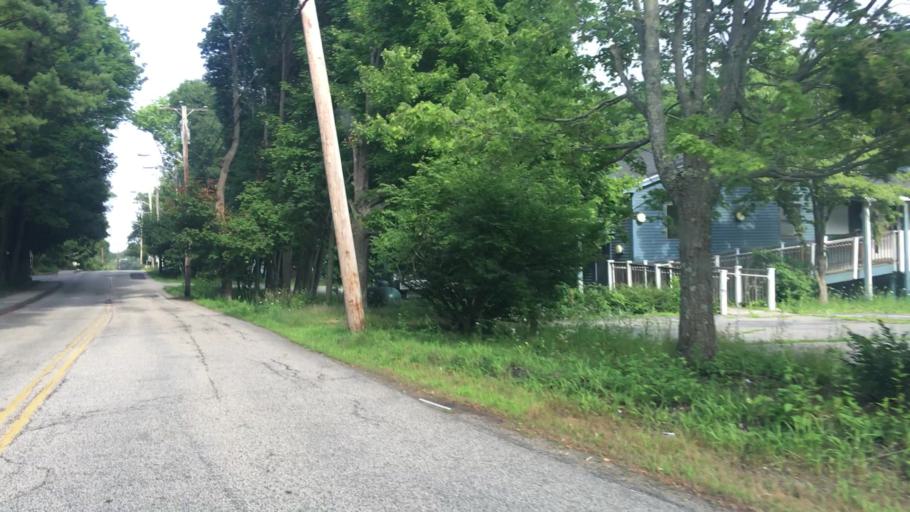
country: US
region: Maine
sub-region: York County
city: Kittery
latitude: 43.0919
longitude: -70.7368
